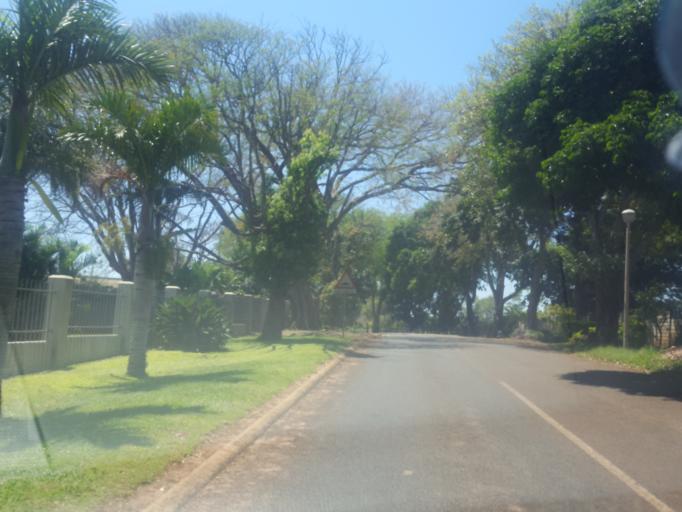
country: ZA
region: KwaZulu-Natal
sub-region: uThungulu District Municipality
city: Empangeni
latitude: -28.7497
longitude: 31.9035
